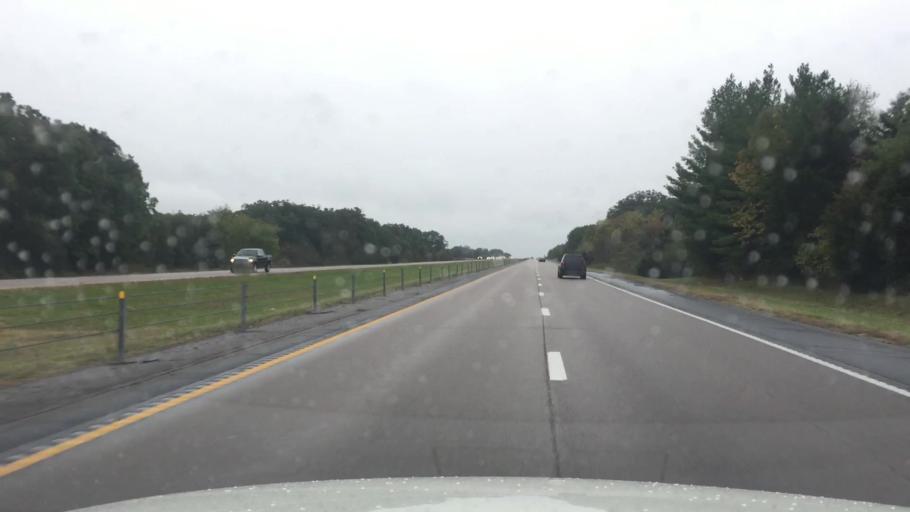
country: US
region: Missouri
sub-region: Boone County
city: Ashland
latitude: 38.7281
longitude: -92.2543
